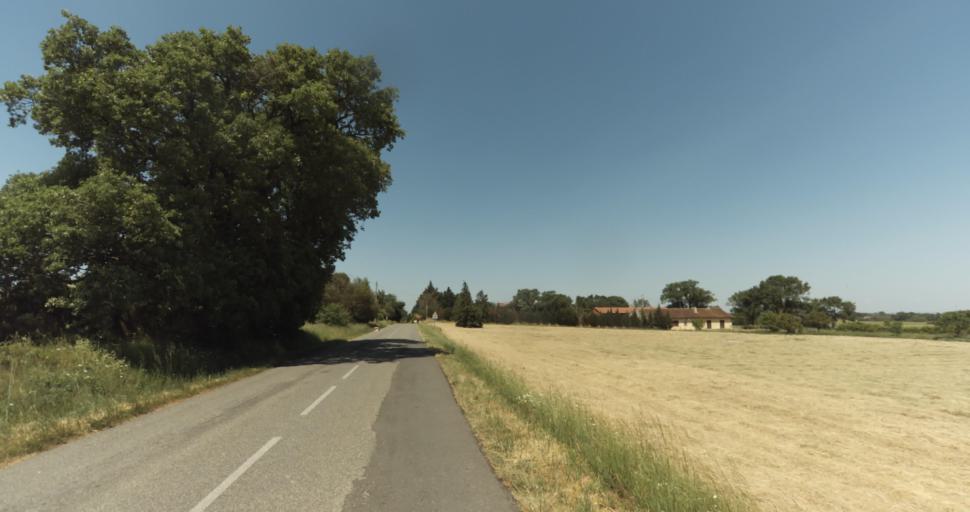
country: FR
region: Midi-Pyrenees
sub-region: Departement de la Haute-Garonne
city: Levignac
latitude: 43.6313
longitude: 1.1812
